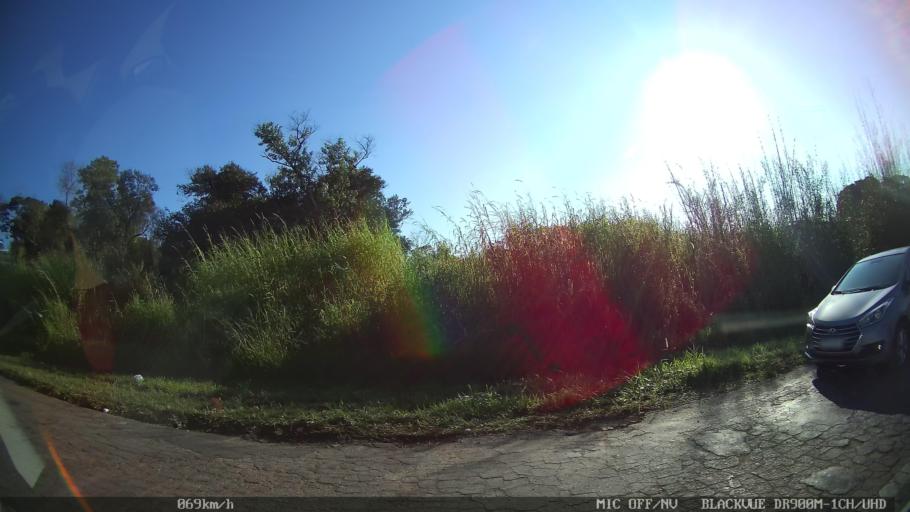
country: BR
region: Sao Paulo
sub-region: Vinhedo
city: Vinhedo
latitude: -23.0539
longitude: -47.0615
